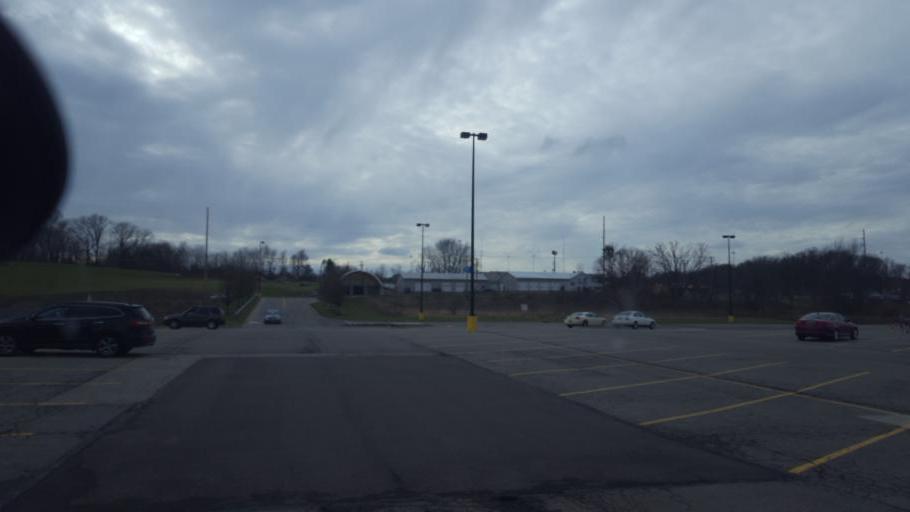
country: US
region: Ohio
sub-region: Richland County
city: Mansfield
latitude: 40.6906
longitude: -82.5091
